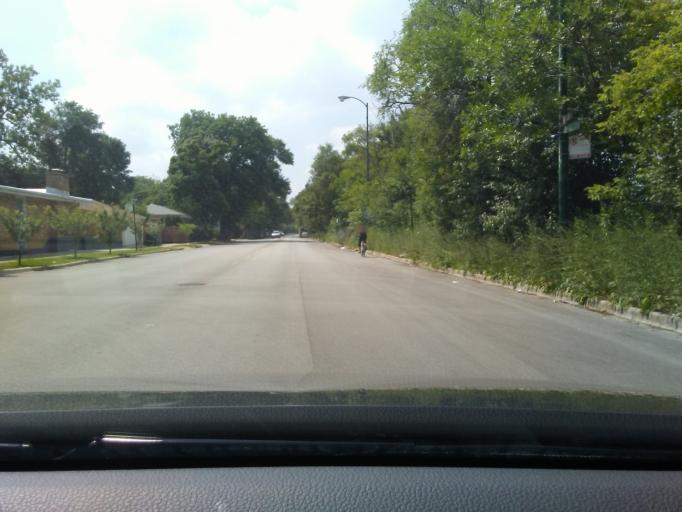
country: US
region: Illinois
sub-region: Cook County
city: Lincolnwood
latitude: 42.0183
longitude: -87.7087
